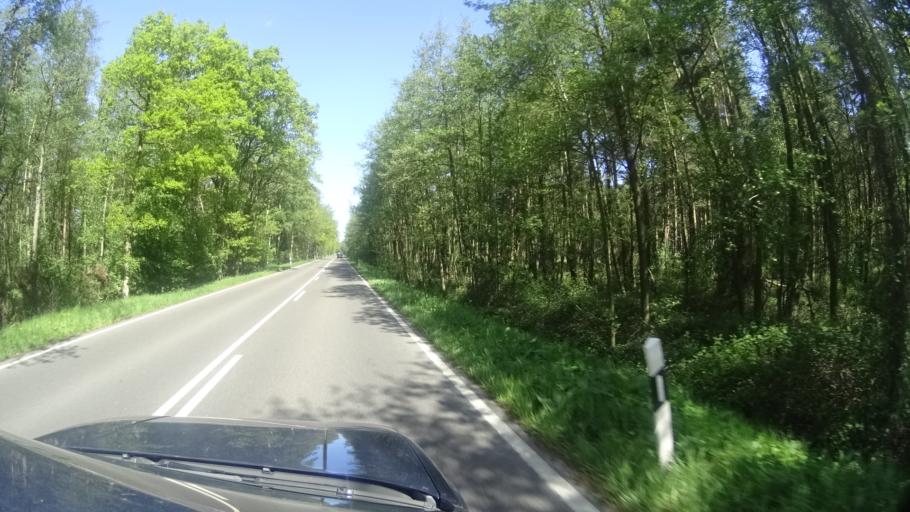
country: DE
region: Mecklenburg-Vorpommern
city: Zingst
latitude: 54.4357
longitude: 12.6517
